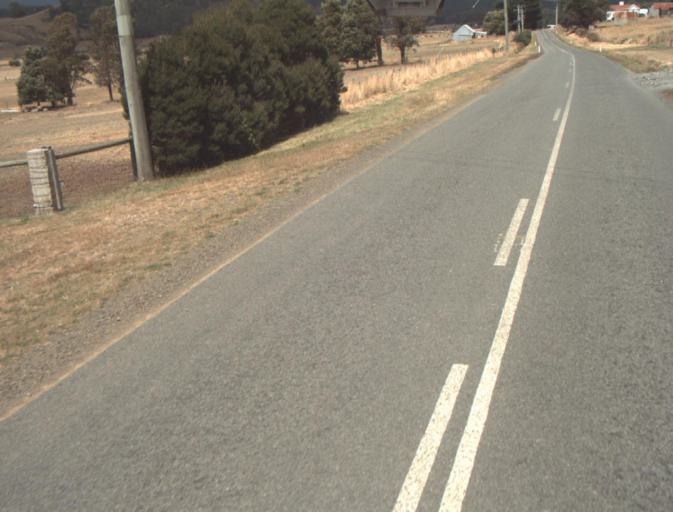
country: AU
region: Tasmania
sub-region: Launceston
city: Mayfield
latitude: -41.2386
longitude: 147.1349
